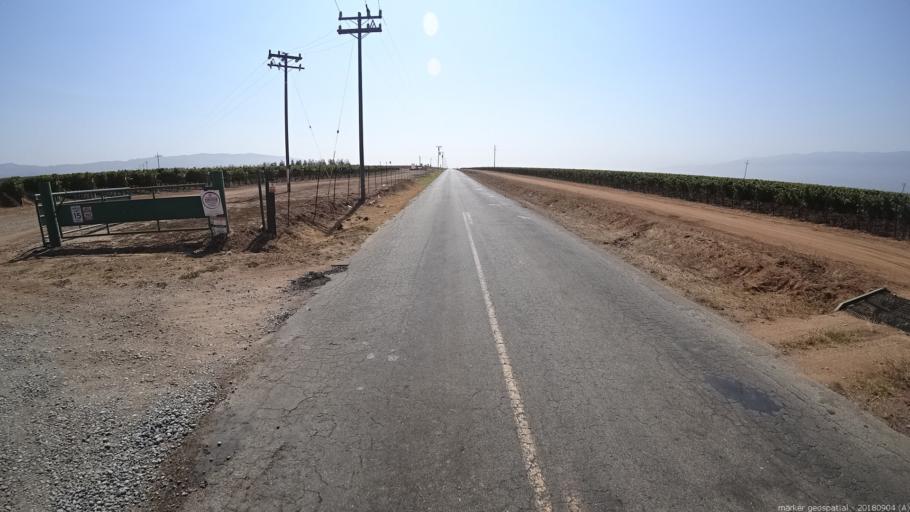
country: US
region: California
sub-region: Monterey County
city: Gonzales
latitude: 36.5129
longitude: -121.4088
